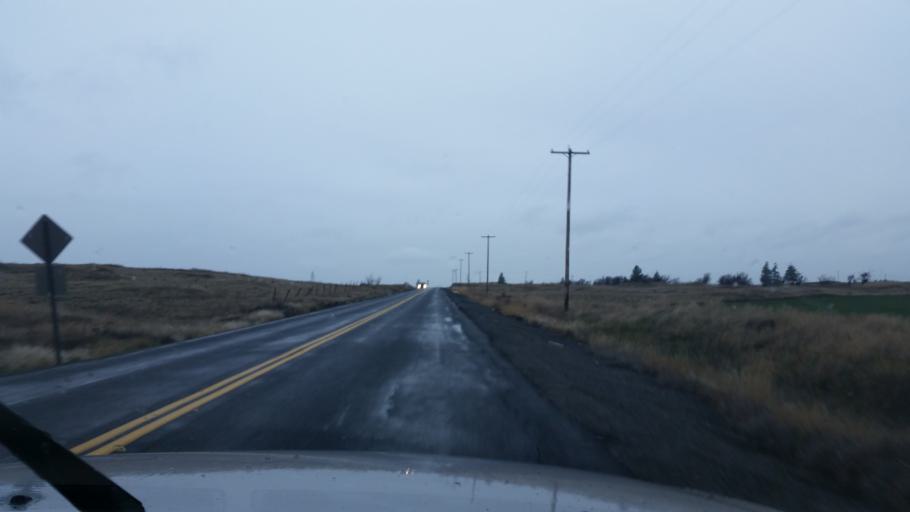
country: US
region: Washington
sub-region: Spokane County
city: Airway Heights
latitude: 47.6865
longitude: -117.5640
